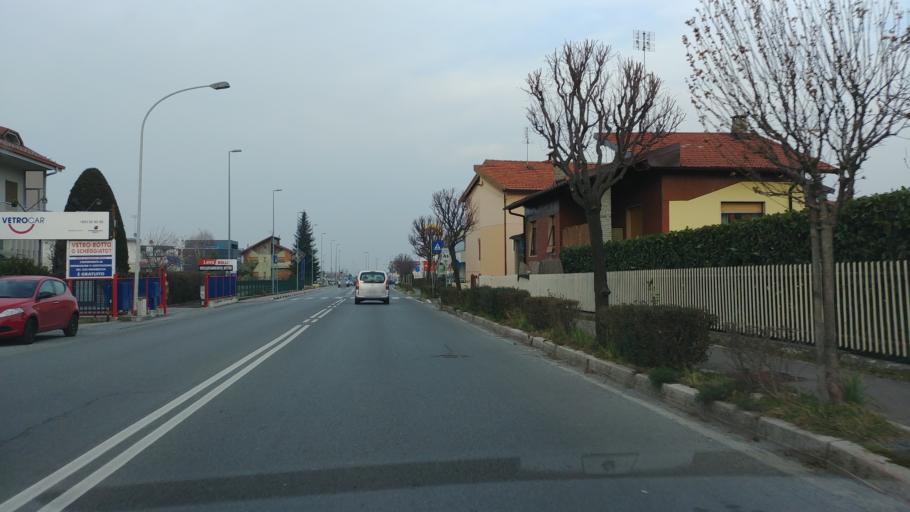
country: IT
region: Piedmont
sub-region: Provincia di Cuneo
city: Borgo San Dalmazzo
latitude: 44.3452
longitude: 7.5024
